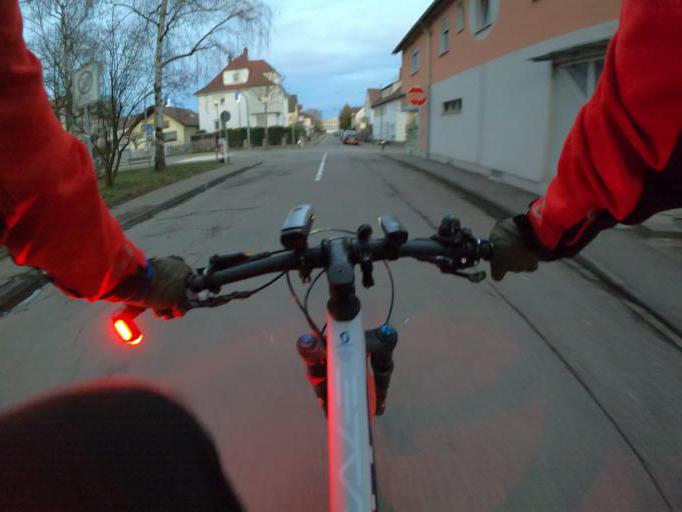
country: DE
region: Baden-Wuerttemberg
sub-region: Regierungsbezirk Stuttgart
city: Reichenbach an der Fils
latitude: 48.7111
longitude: 9.4656
